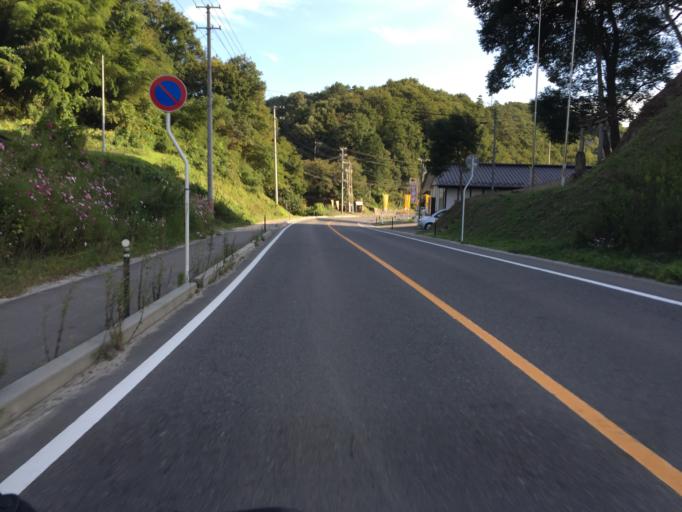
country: JP
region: Fukushima
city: Hobaramachi
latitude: 37.6791
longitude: 140.6158
